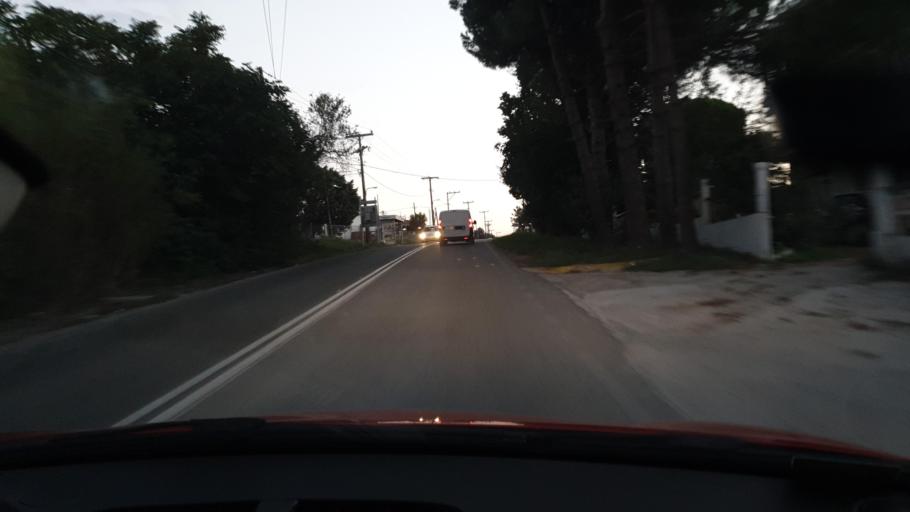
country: GR
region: Central Macedonia
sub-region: Nomos Thessalonikis
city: Agia Triada
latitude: 40.4962
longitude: 22.8731
